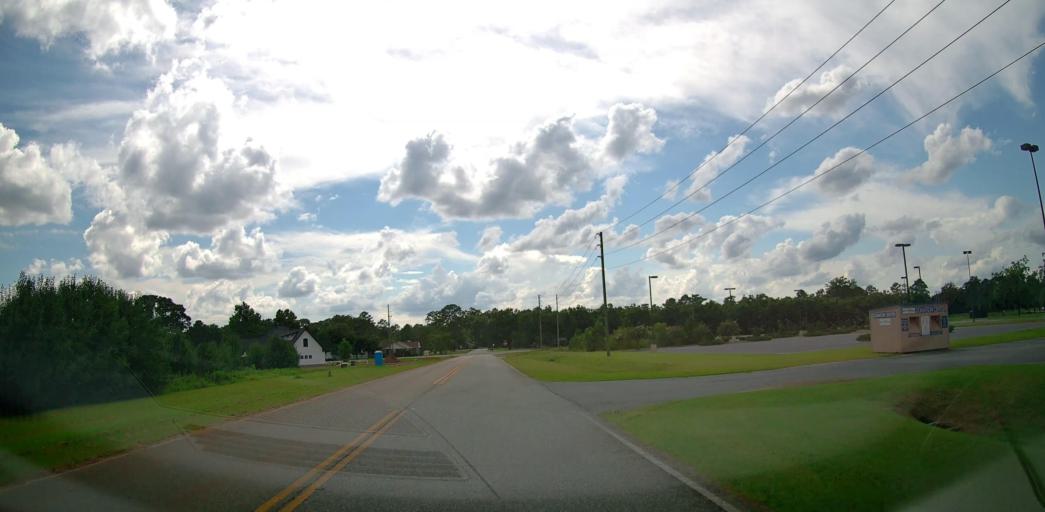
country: US
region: Georgia
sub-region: Houston County
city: Centerville
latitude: 32.5839
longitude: -83.6647
